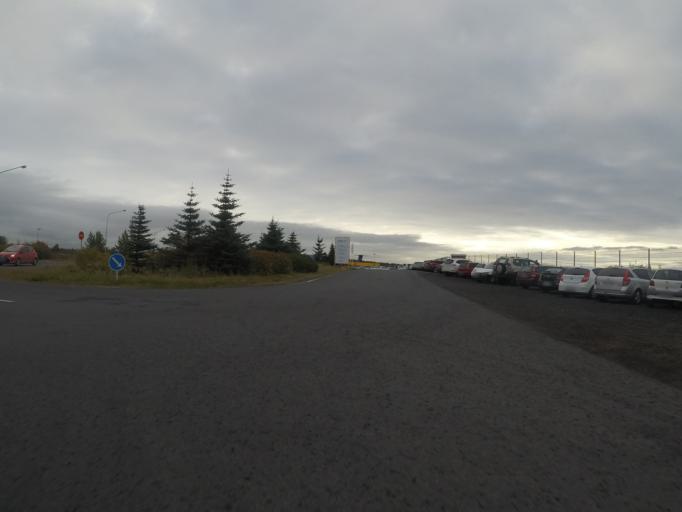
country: IS
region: Capital Region
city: Kopavogur
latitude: 64.1324
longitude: -21.9499
